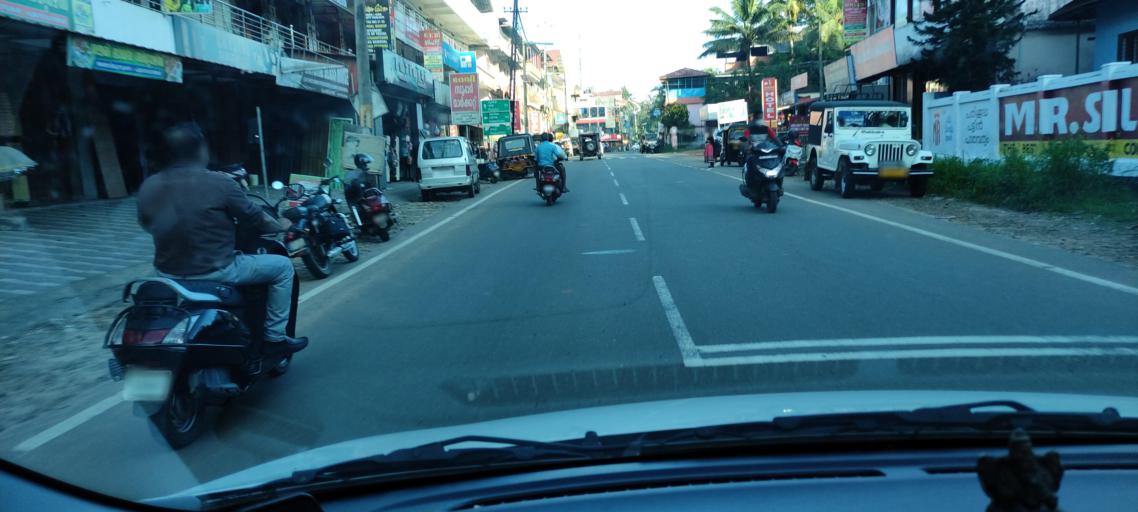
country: IN
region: Kerala
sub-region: Pattanamtitta
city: Adur
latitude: 9.1450
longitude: 76.7681
